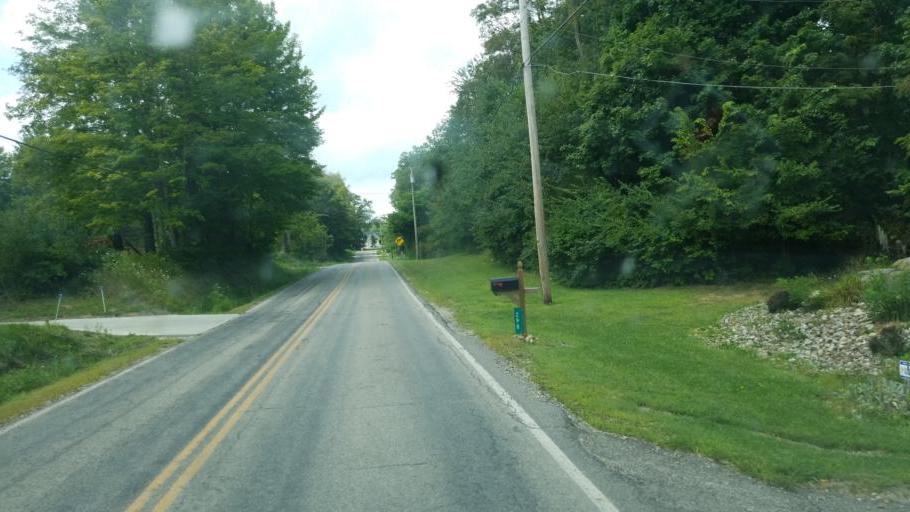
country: US
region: Ohio
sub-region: Richland County
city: Ontario
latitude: 40.7513
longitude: -82.6401
